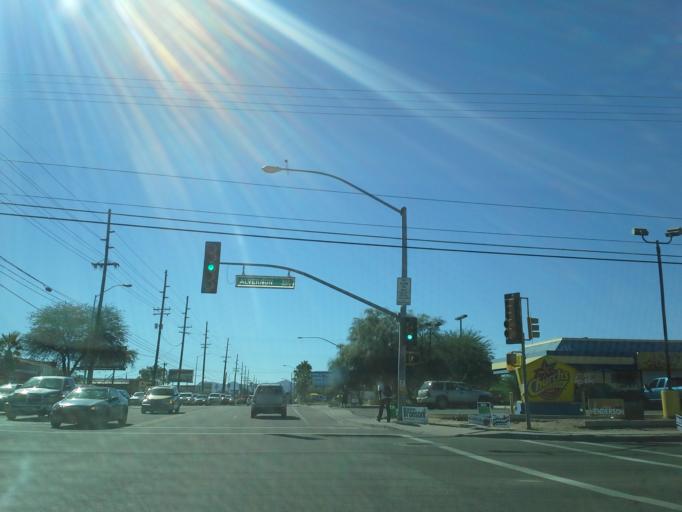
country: US
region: Arizona
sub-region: Pima County
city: Tucson
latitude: 32.2507
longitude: -110.9096
